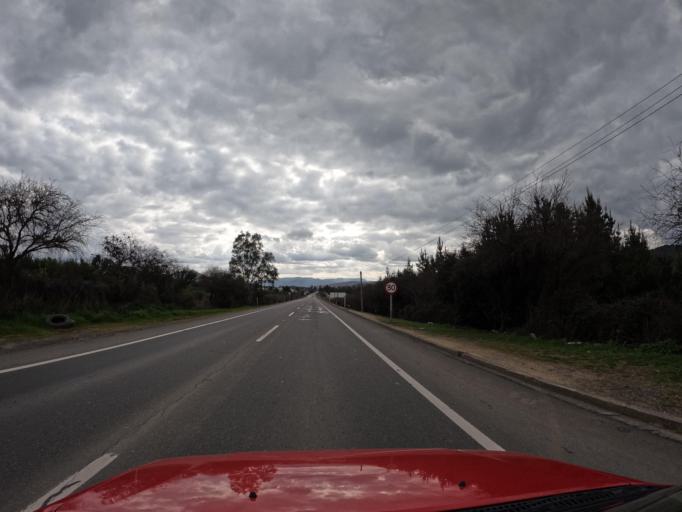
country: CL
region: Maule
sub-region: Provincia de Linares
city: San Javier
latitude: -35.6143
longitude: -71.7842
